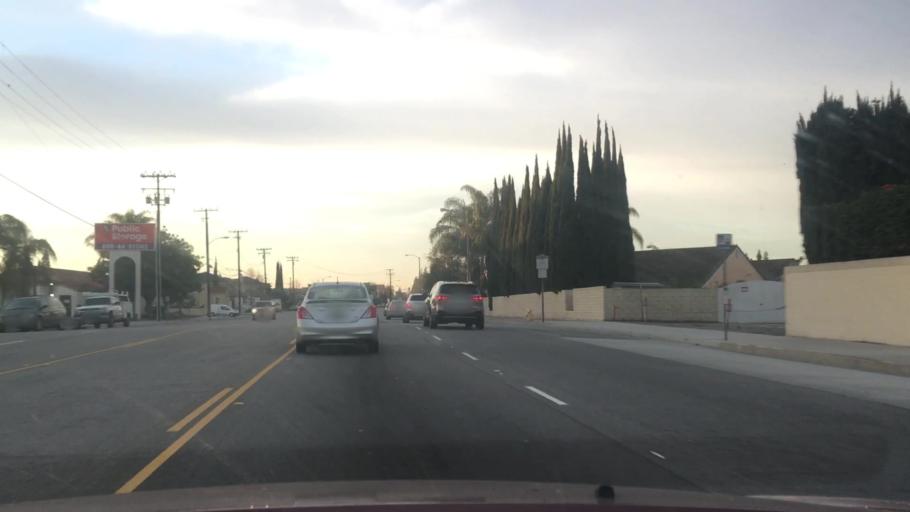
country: US
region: California
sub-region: Orange County
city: Stanton
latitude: 33.8066
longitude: -118.0107
